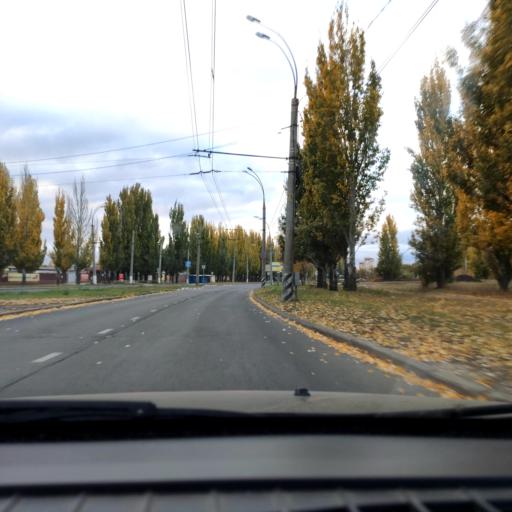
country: RU
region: Samara
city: Tol'yatti
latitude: 53.5428
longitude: 49.2789
